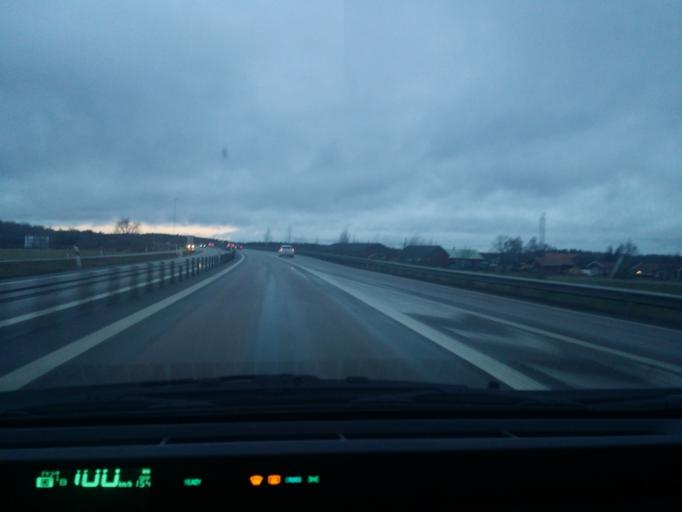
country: SE
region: Soedermanland
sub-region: Eskilstuna Kommun
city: Hallbybrunn
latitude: 59.4057
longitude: 16.4181
